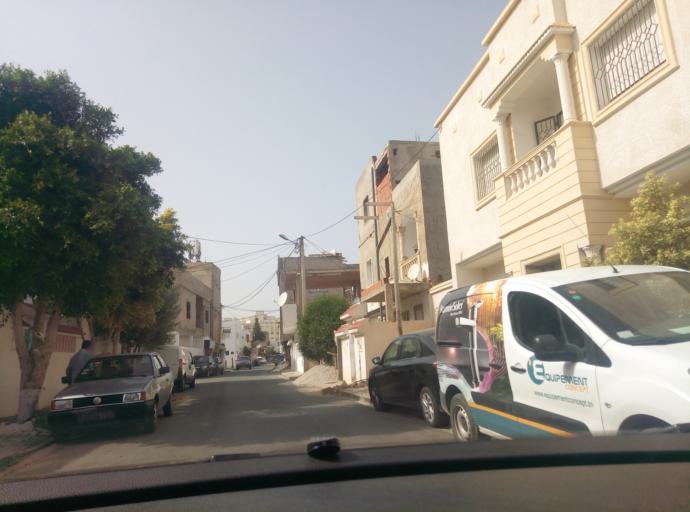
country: TN
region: Tunis
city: La Goulette
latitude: 36.8540
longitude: 10.2709
